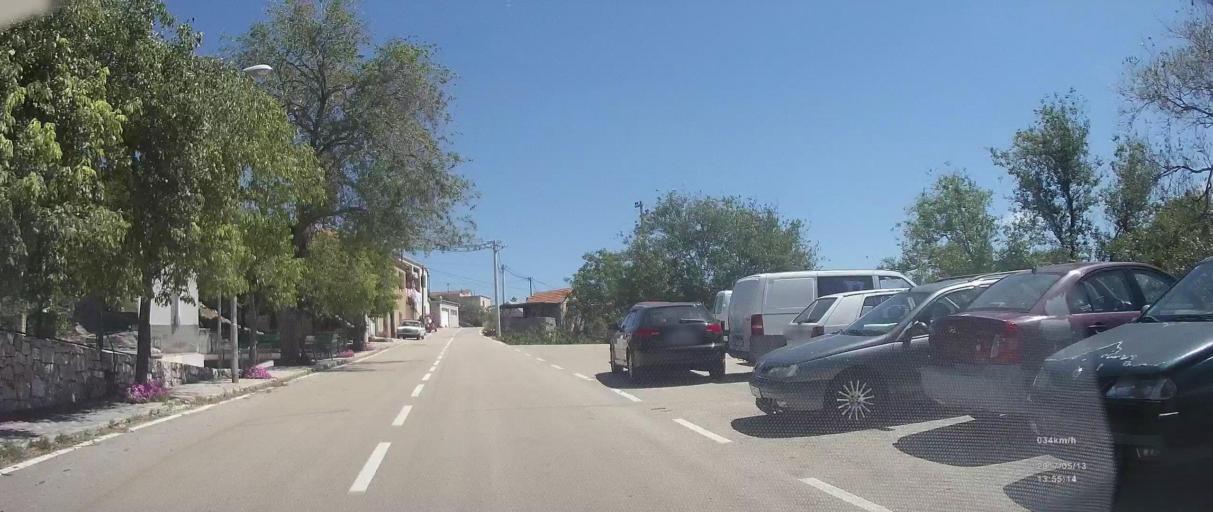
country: HR
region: Sibensko-Kniniska
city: Rogoznica
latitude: 43.5955
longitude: 16.0134
